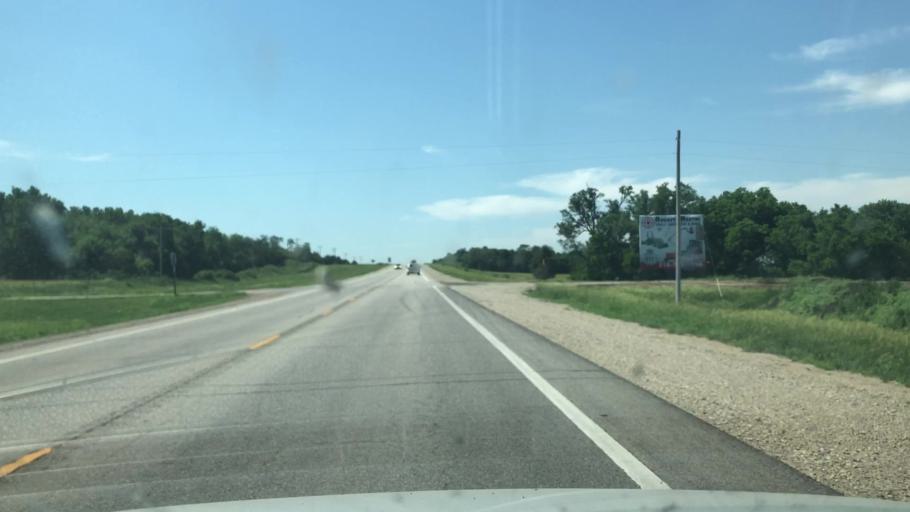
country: US
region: Kansas
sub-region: Cowley County
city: Winfield
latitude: 37.3761
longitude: -97.0070
